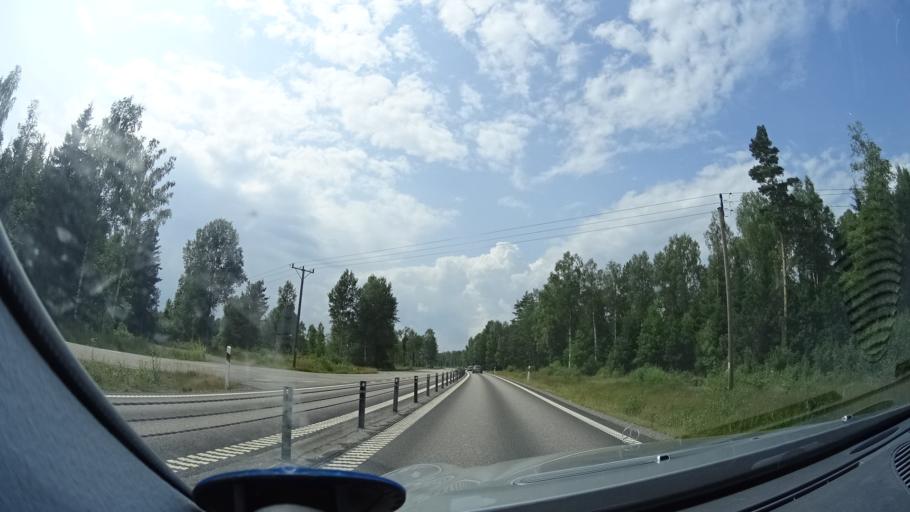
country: SE
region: Kalmar
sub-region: Nybro Kommun
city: Nybro
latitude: 56.7339
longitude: 15.8504
